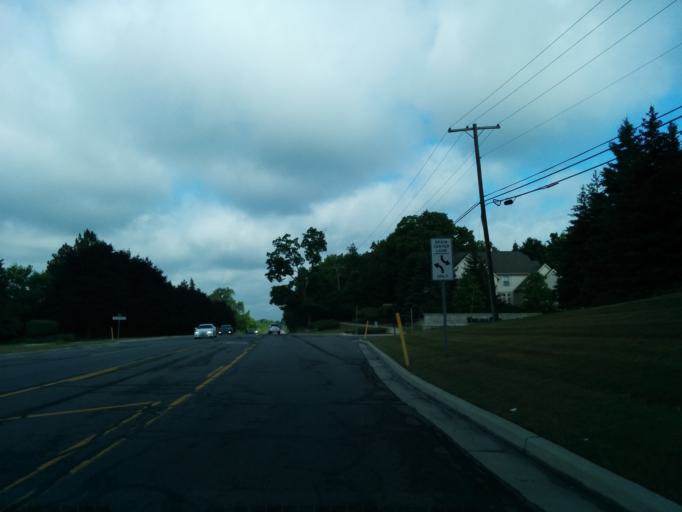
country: US
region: Michigan
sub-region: Oakland County
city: West Bloomfield Township
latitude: 42.5270
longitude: -83.4110
